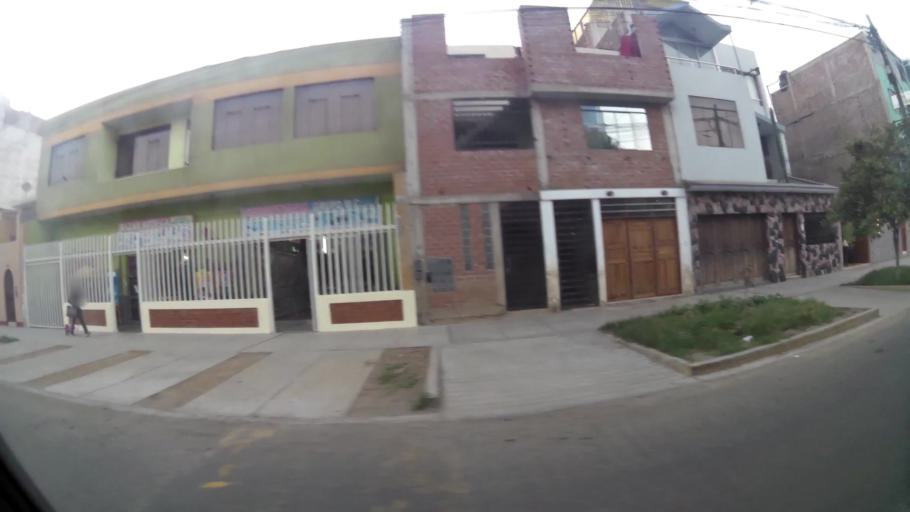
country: PE
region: La Libertad
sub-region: Provincia de Trujillo
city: Trujillo
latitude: -8.1003
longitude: -79.0216
